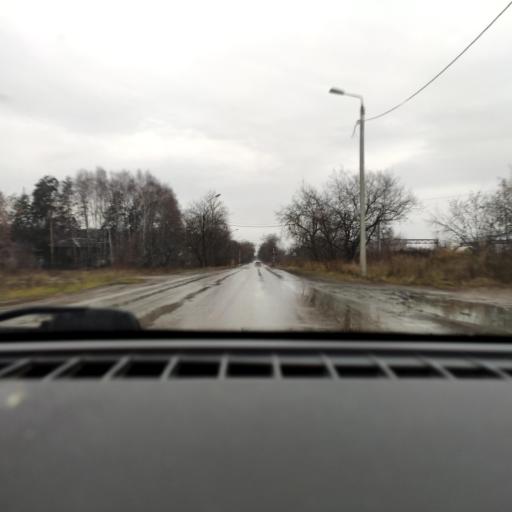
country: RU
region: Perm
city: Kultayevo
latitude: 57.9931
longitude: 55.9228
